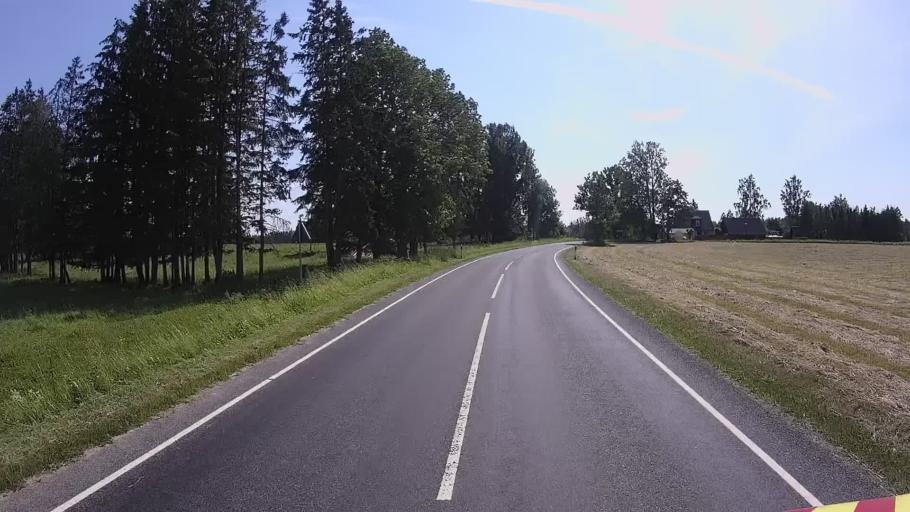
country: EE
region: Viljandimaa
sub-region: Karksi vald
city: Karksi-Nuia
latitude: 58.0588
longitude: 25.5504
